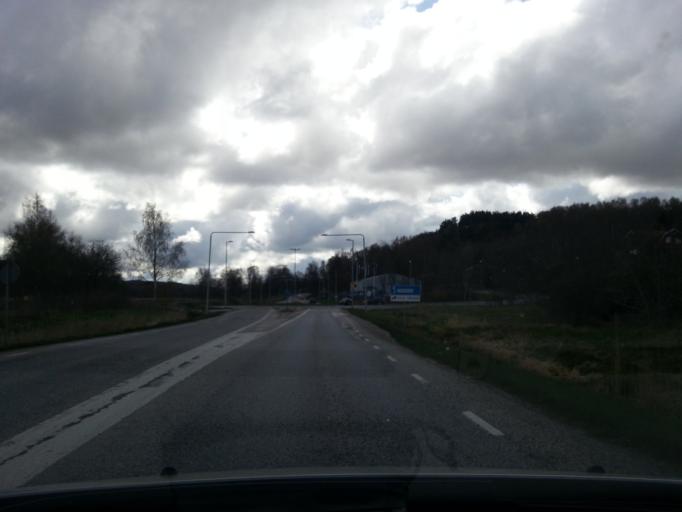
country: SE
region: Vaestra Goetaland
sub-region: Goteborg
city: Goeteborg
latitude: 57.7604
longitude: 11.9385
